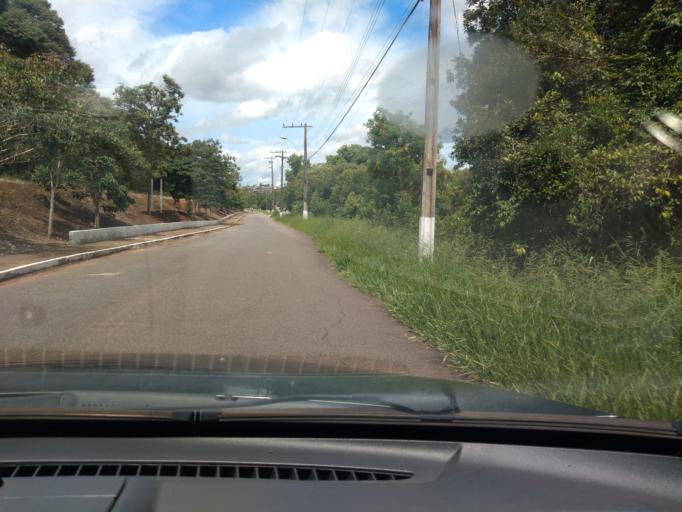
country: BR
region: Minas Gerais
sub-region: Tres Coracoes
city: Tres Coracoes
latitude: -21.7009
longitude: -45.2712
